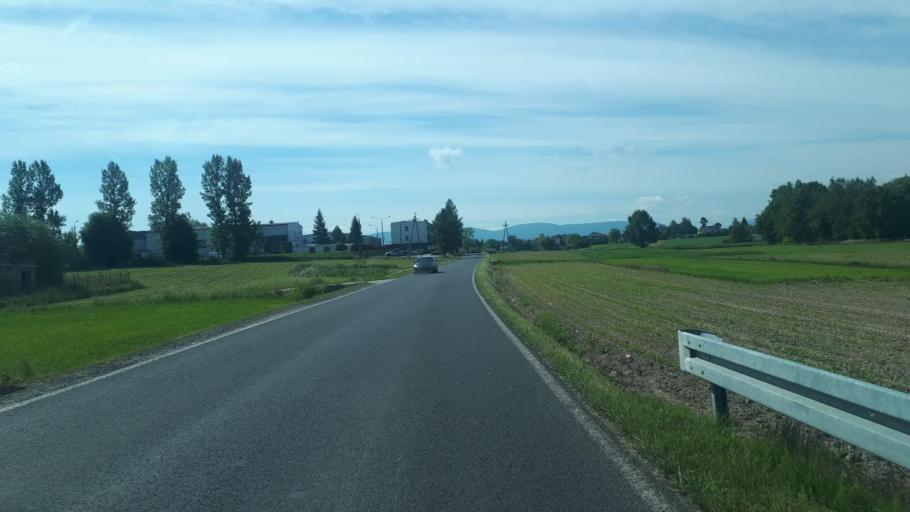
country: PL
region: Silesian Voivodeship
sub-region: Powiat bielski
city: Wilamowice
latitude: 49.9271
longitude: 19.1494
